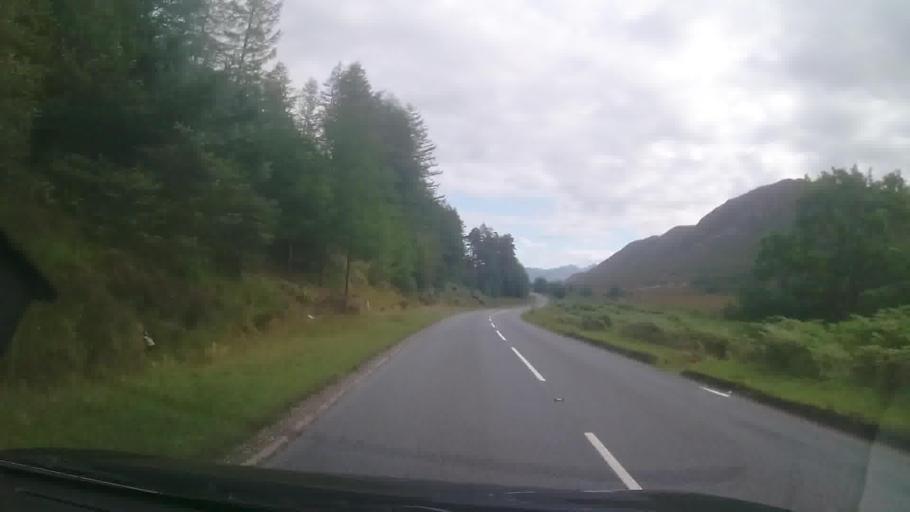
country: GB
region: Scotland
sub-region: Argyll and Bute
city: Oban
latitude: 56.6884
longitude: -5.4668
